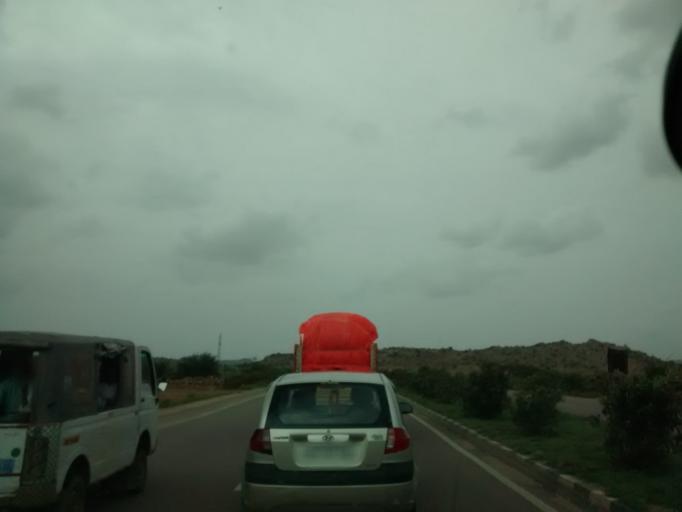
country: IN
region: Andhra Pradesh
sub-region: Kurnool
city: Ramapuram
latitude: 15.1773
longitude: 77.6863
